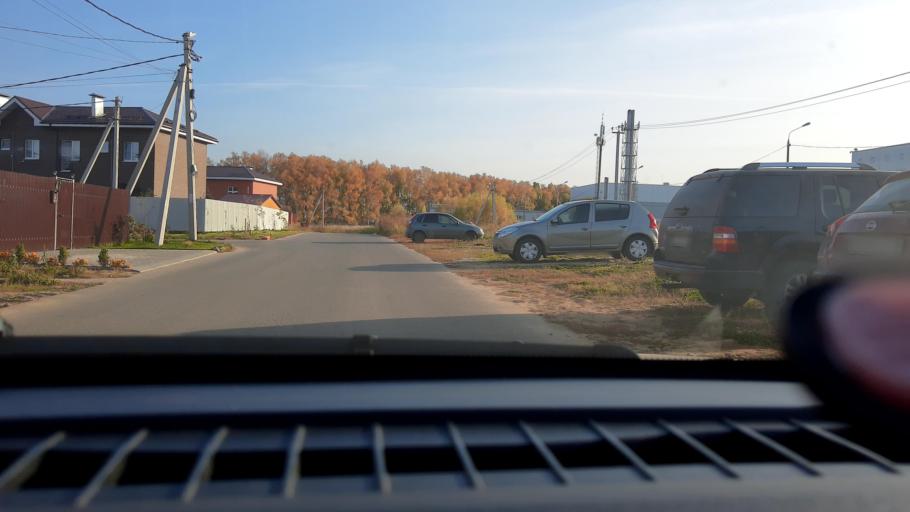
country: RU
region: Nizjnij Novgorod
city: Afonino
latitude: 56.2147
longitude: 44.0846
